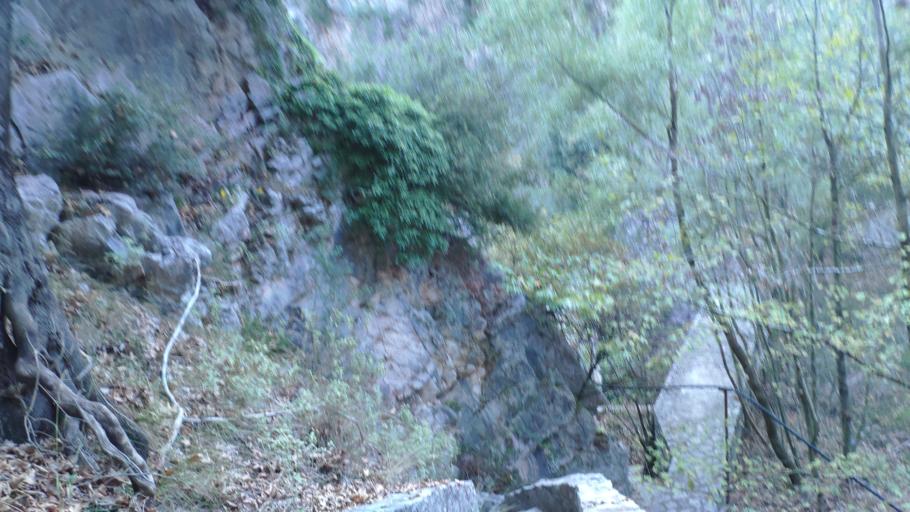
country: GR
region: Thessaly
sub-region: Trikala
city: Pyli
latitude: 39.4313
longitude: 21.5272
